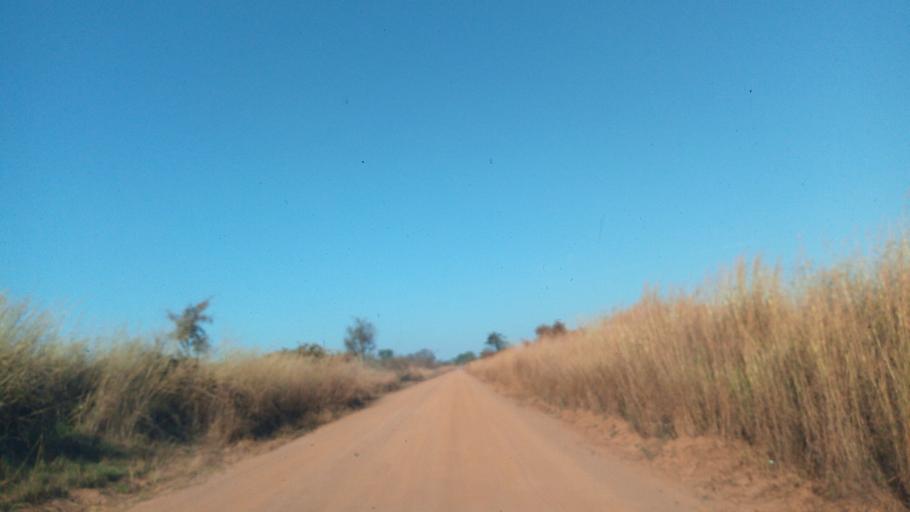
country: ZM
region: Luapula
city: Mwense
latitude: -10.5139
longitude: 28.4642
